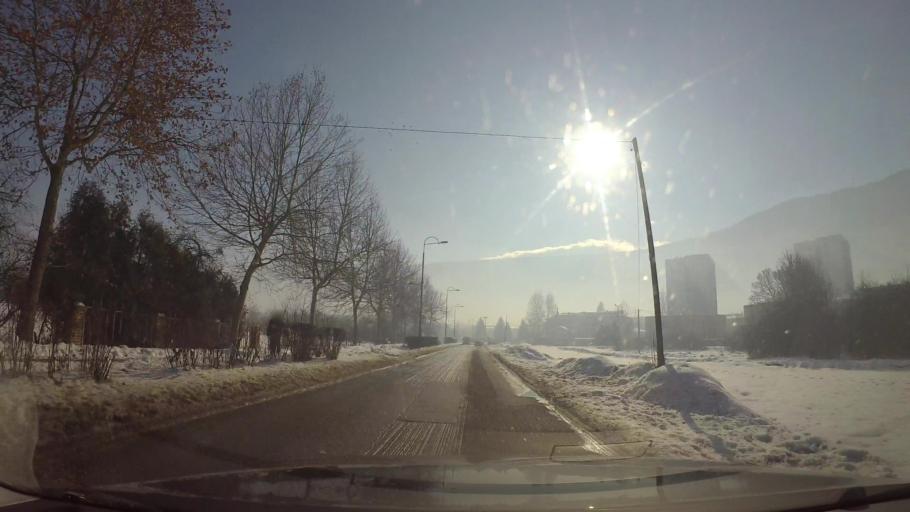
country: BA
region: Federation of Bosnia and Herzegovina
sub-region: Kanton Sarajevo
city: Sarajevo
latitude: 43.8003
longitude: 18.3131
